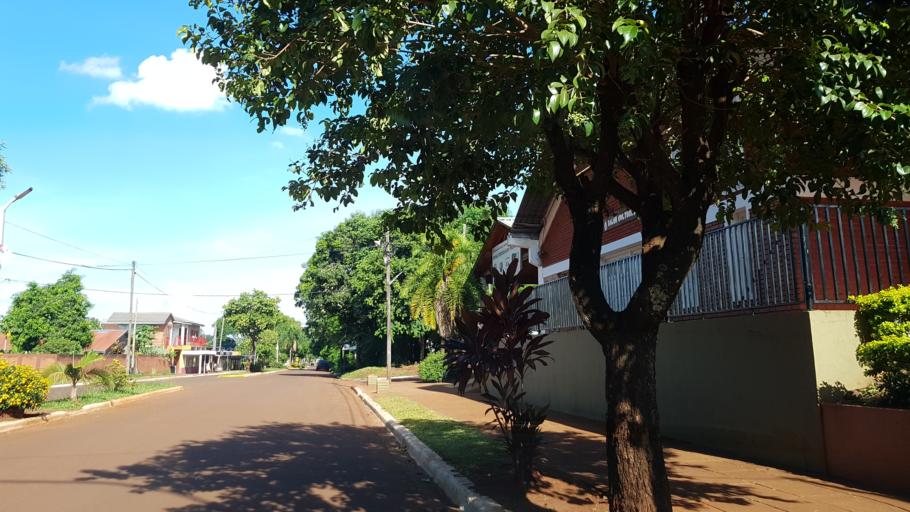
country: AR
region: Misiones
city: Puerto Libertad
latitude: -25.9220
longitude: -54.5845
